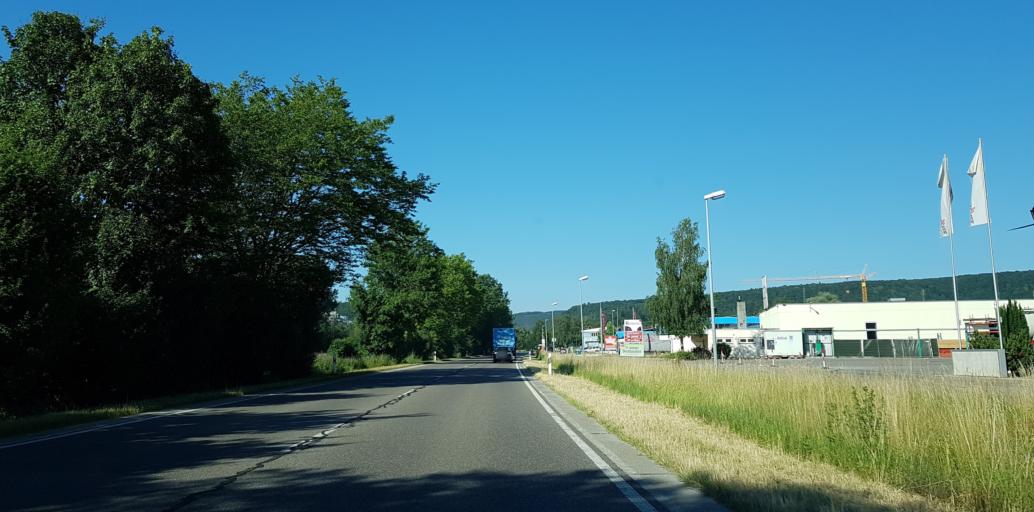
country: DE
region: Baden-Wuerttemberg
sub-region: Tuebingen Region
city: Schelklingen
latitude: 48.3781
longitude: 9.7459
